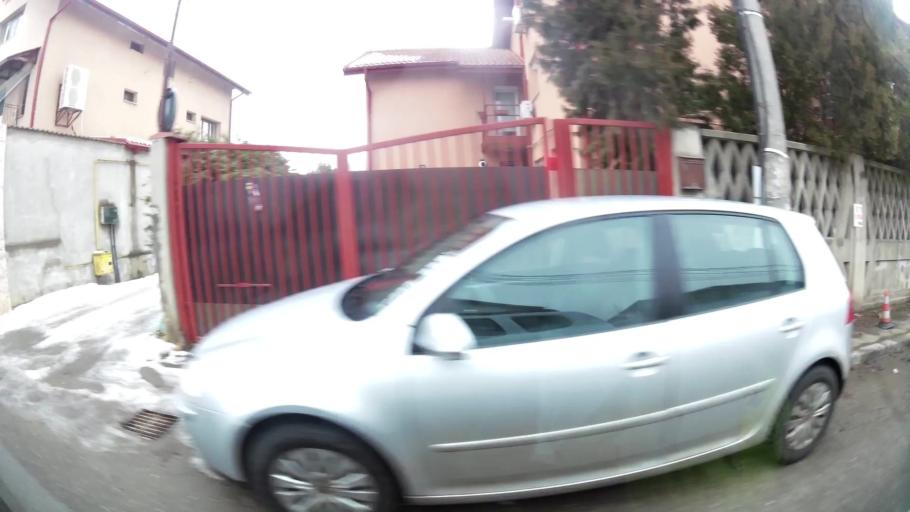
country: RO
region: Ilfov
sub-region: Comuna Chiajna
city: Rosu
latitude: 44.4478
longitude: 26.0060
